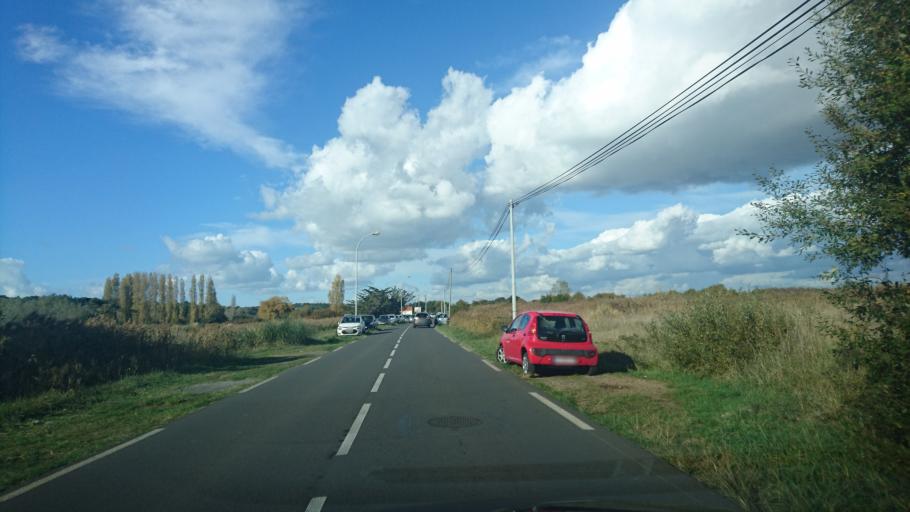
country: FR
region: Pays de la Loire
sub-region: Departement de la Vendee
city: Les Sables-d'Olonne
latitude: 46.5107
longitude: -1.8034
